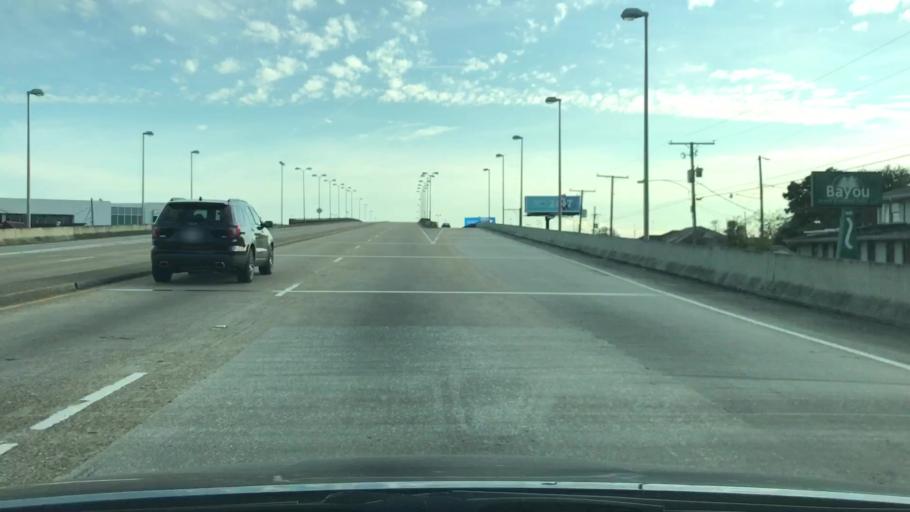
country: US
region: Louisiana
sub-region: Jefferson Parish
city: Metairie
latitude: 29.9779
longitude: -90.1563
